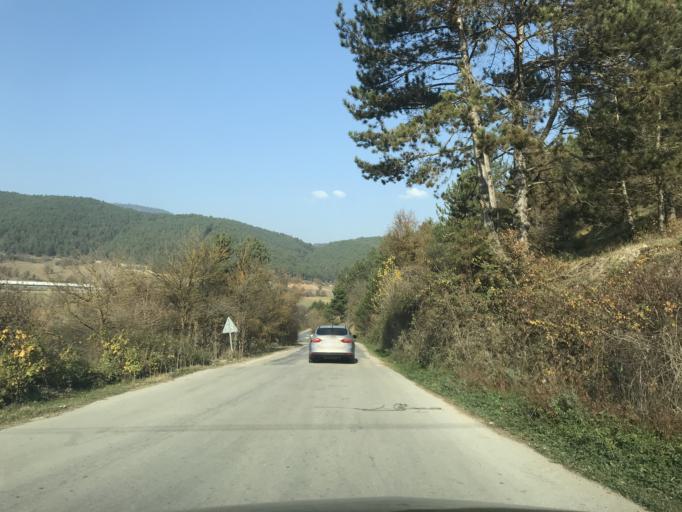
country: TR
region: Bolu
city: Bolu
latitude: 40.7867
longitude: 31.6362
